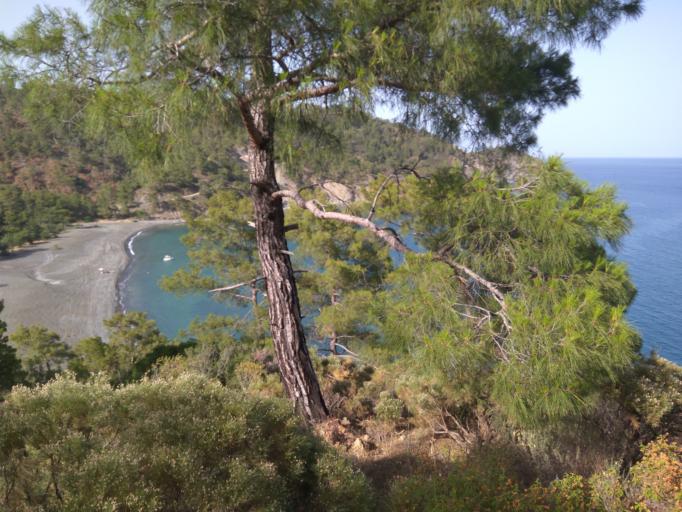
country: TR
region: Antalya
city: Tekirova
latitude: 36.4661
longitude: 30.5058
